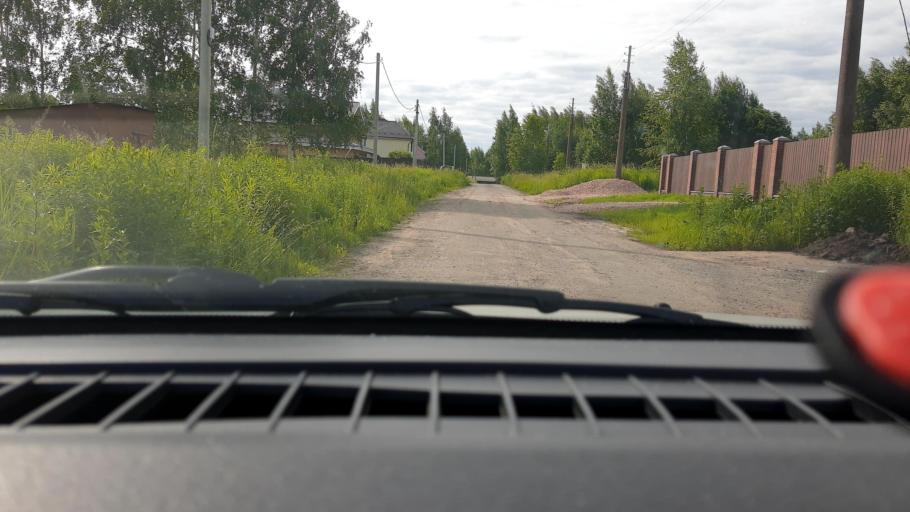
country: RU
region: Nizjnij Novgorod
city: Afonino
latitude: 56.2489
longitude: 44.0696
